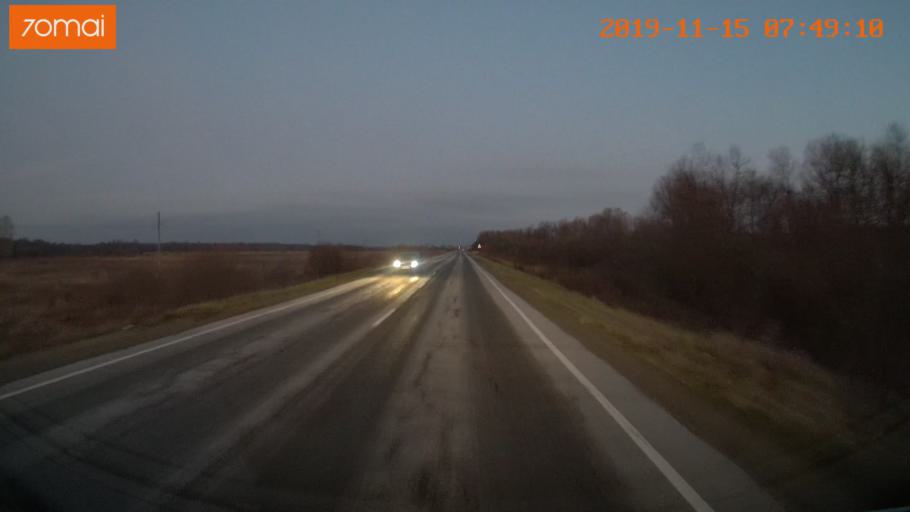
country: RU
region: Vologda
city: Cherepovets
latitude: 58.8566
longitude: 38.2360
